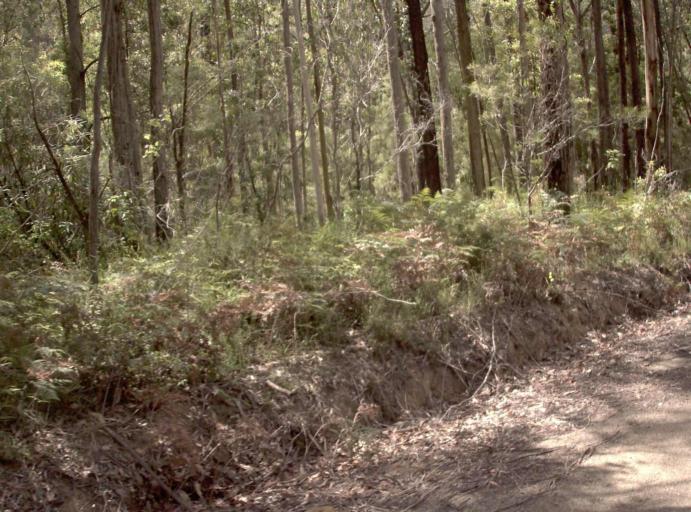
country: AU
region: New South Wales
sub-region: Bombala
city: Bombala
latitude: -37.5378
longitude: 149.3683
